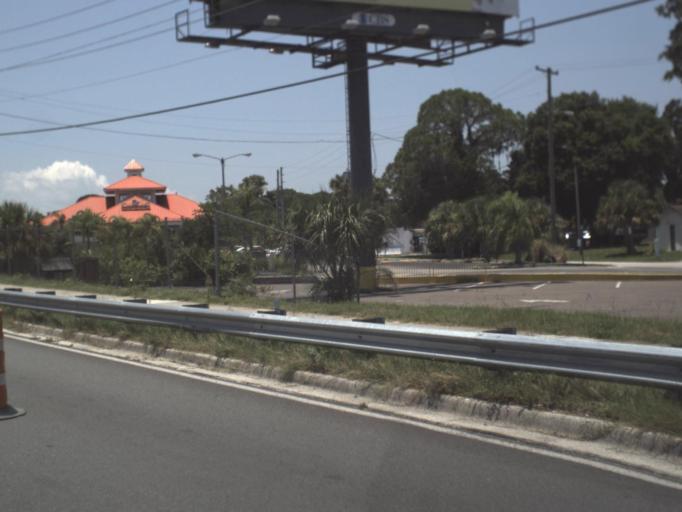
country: US
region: Florida
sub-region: Pasco County
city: Port Richey
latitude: 28.2710
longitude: -82.7246
